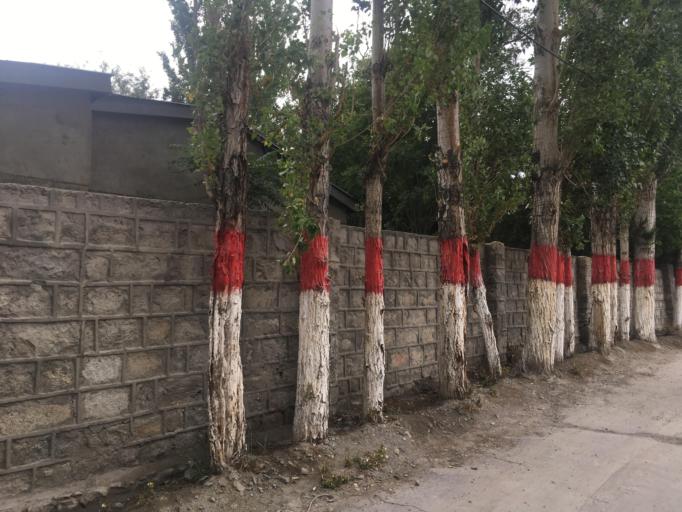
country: PK
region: Gilgit-Baltistan
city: Skardu
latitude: 35.2944
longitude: 75.6497
